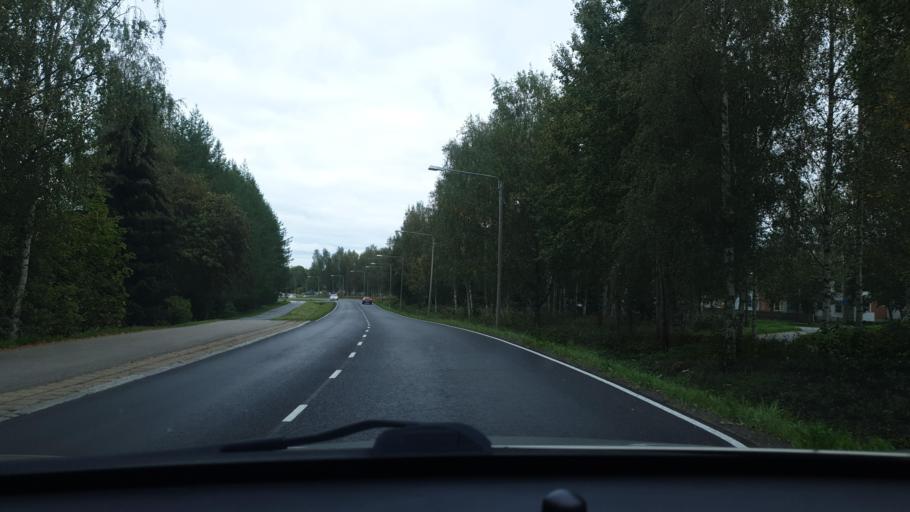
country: FI
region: Ostrobothnia
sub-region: Vaasa
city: Teeriniemi
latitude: 63.0878
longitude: 21.6925
